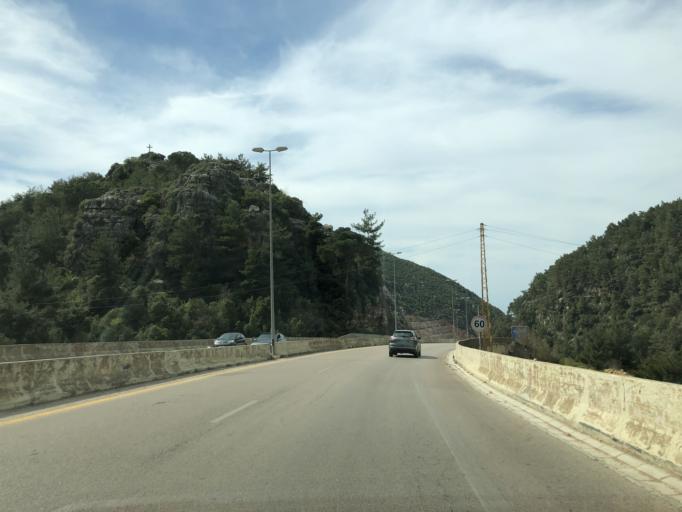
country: LB
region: Mont-Liban
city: Bhamdoun el Mhatta
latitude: 33.8948
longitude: 35.6559
